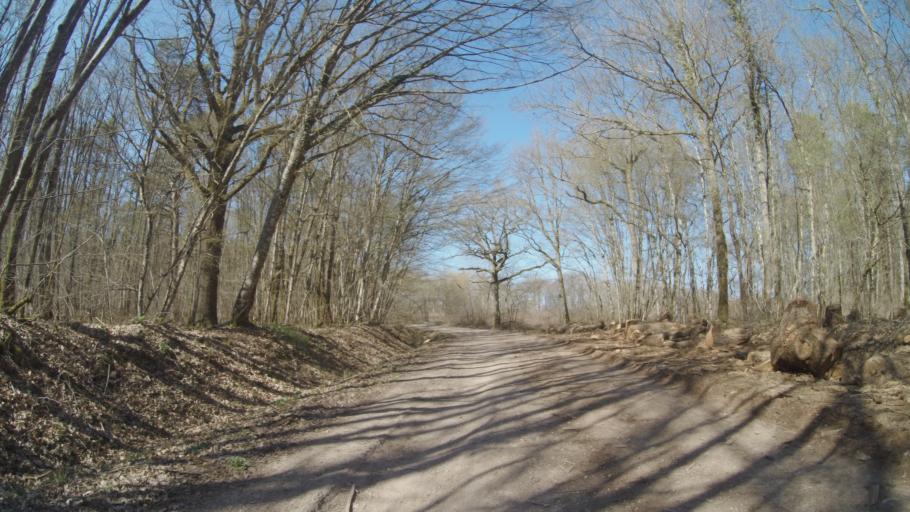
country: FR
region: Centre
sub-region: Departement du Loiret
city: Chanteau
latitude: 47.9592
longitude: 1.9762
